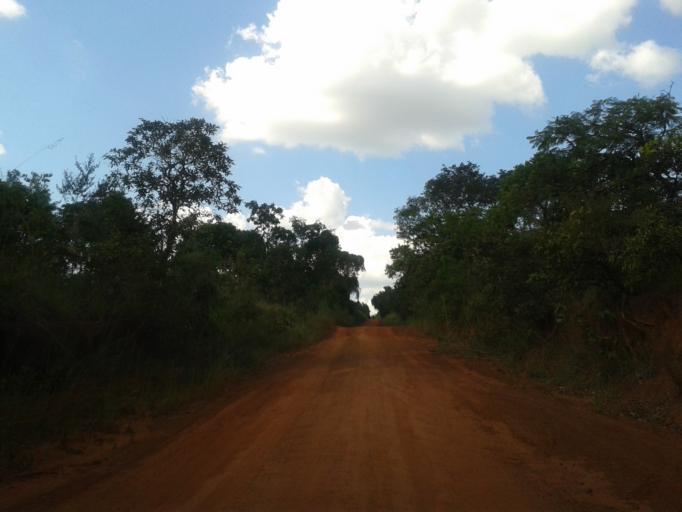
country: BR
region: Minas Gerais
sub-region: Ituiutaba
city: Ituiutaba
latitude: -19.1828
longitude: -49.7266
